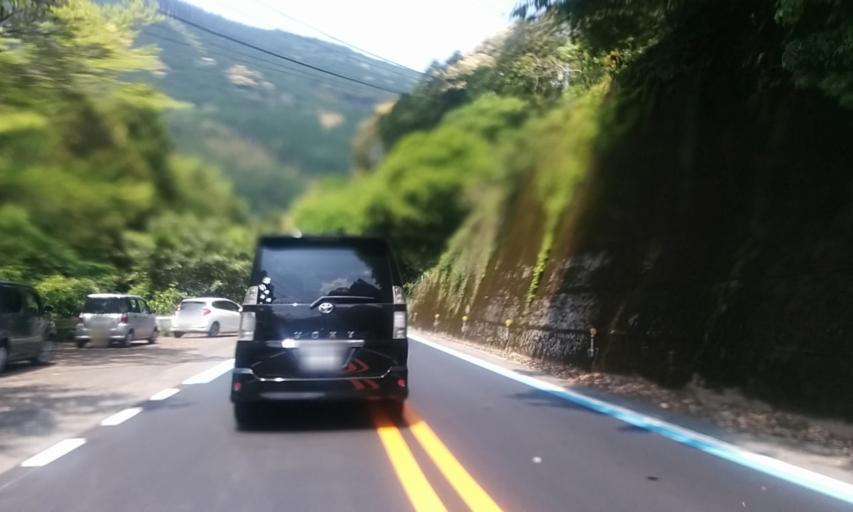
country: JP
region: Ehime
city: Niihama
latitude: 33.9058
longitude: 133.3085
